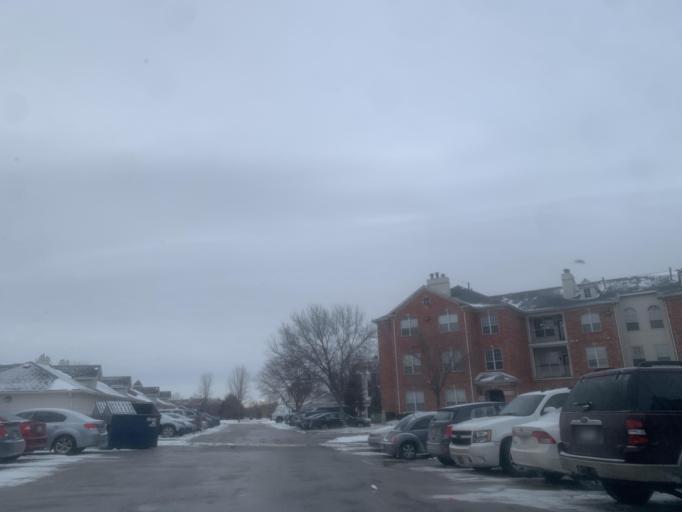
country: US
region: Nebraska
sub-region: Douglas County
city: Ralston
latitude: 41.2733
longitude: -96.0884
